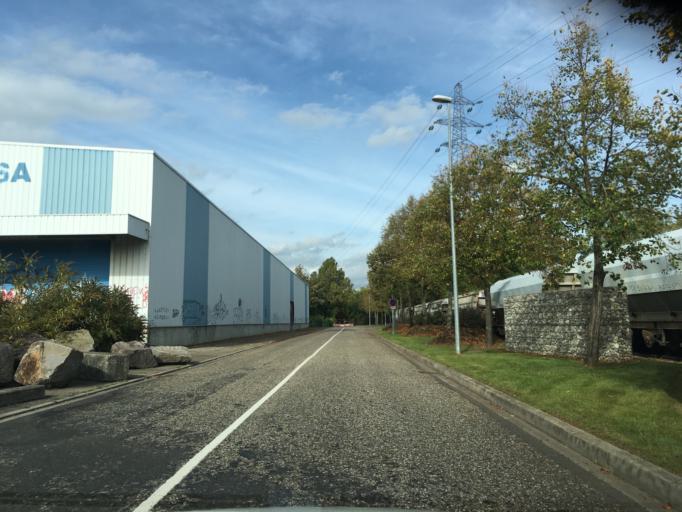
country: DE
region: Baden-Wuerttemberg
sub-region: Freiburg Region
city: Kehl
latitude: 48.5880
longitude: 7.7885
